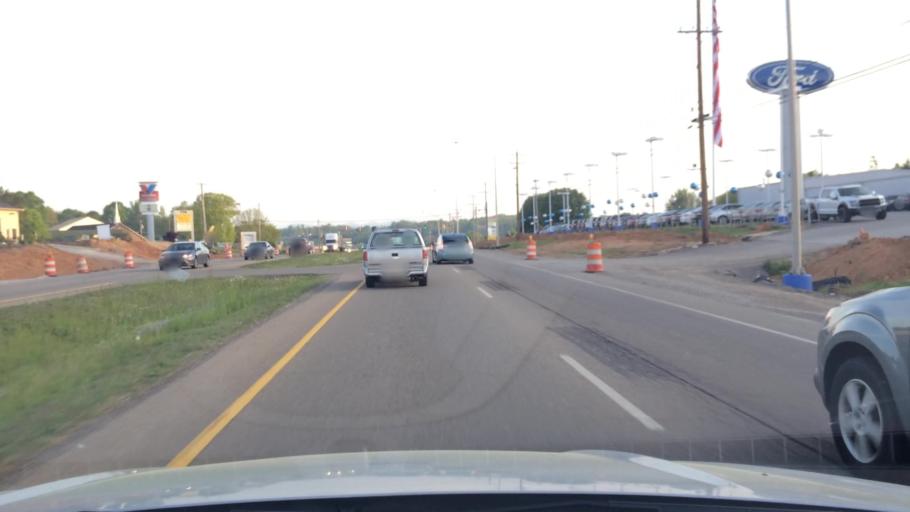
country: US
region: Tennessee
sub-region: Loudon County
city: Lenoir City
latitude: 35.8128
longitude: -84.2637
